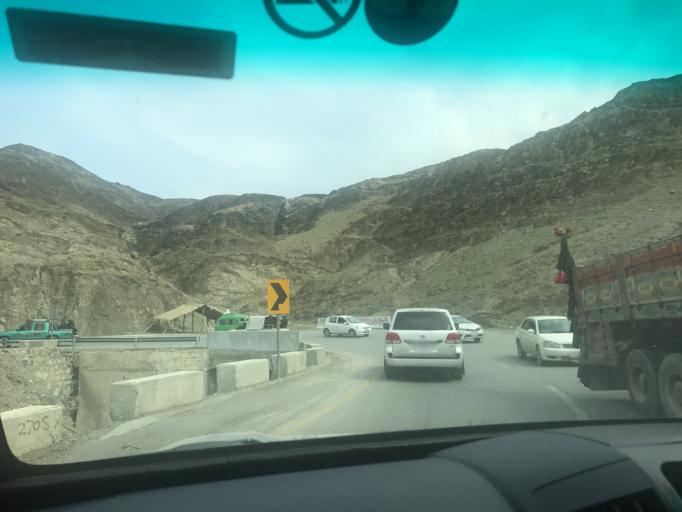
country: PK
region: Federally Administered Tribal Areas
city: Landi Kotal
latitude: 34.1047
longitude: 71.1311
